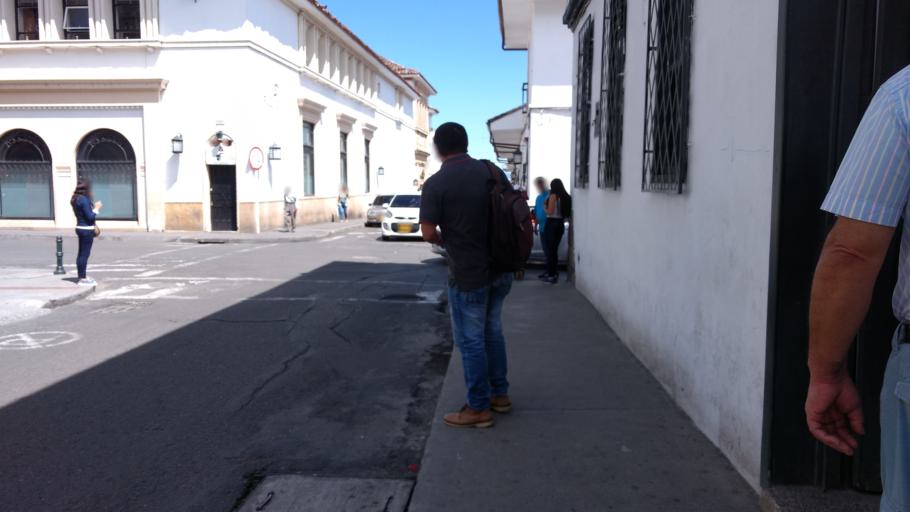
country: CO
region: Cauca
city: Popayan
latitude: 2.4432
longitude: -76.6061
